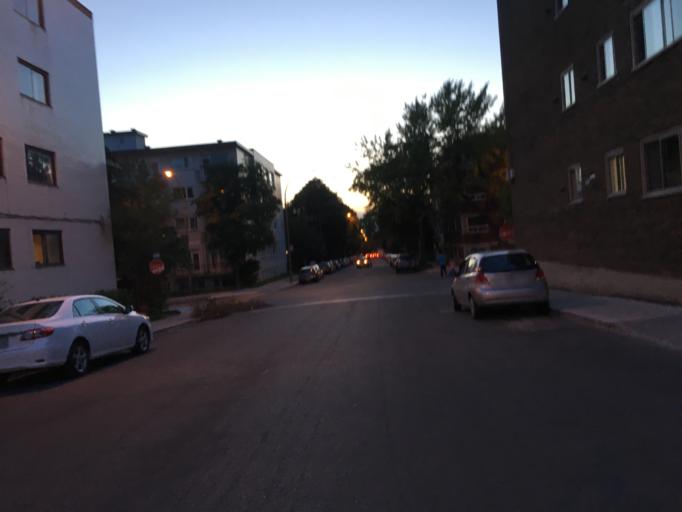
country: CA
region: Quebec
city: Westmount
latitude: 45.4978
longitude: -73.6232
